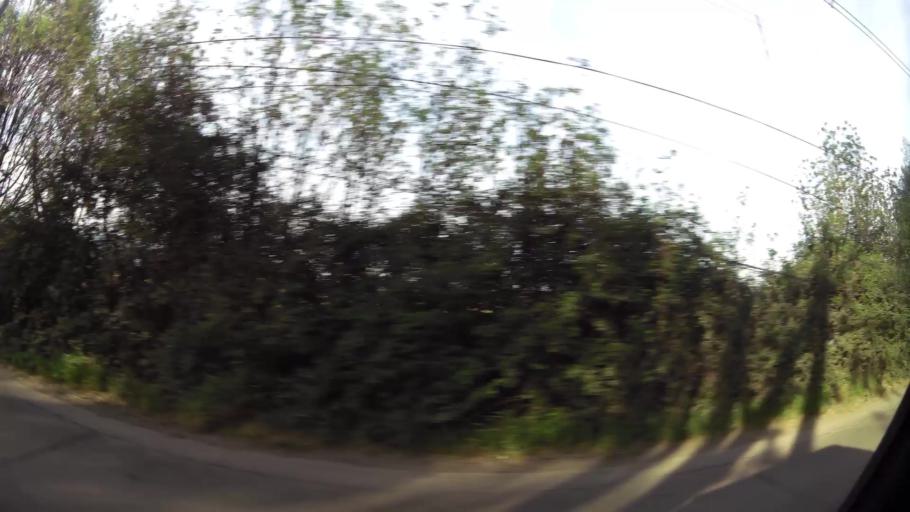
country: CL
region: Santiago Metropolitan
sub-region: Provincia de Maipo
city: San Bernardo
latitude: -33.5597
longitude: -70.7687
